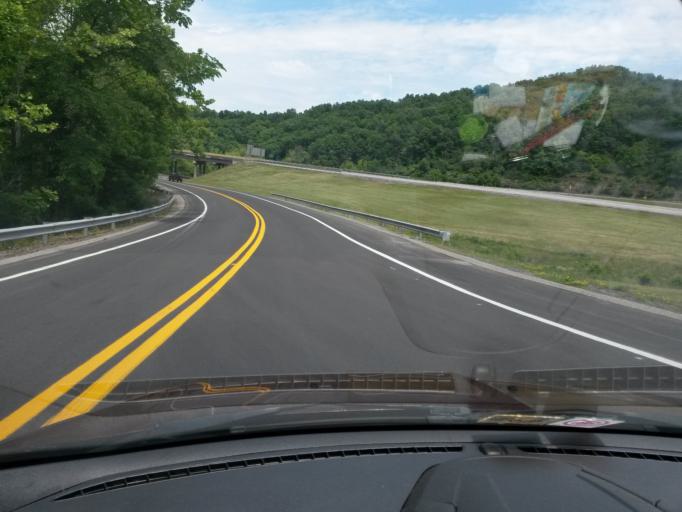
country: US
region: West Virginia
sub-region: Lewis County
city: Weston
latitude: 39.0131
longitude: -80.4693
